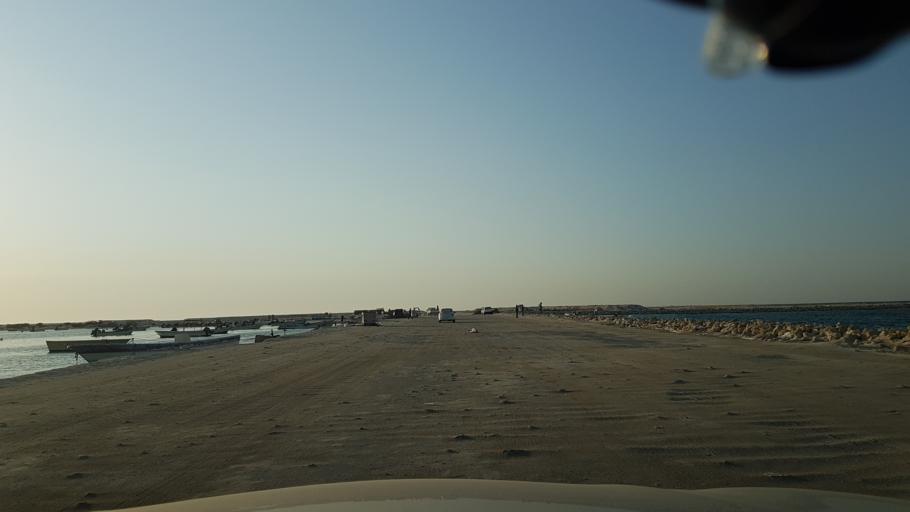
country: BH
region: Manama
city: Jidd Hafs
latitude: 26.2534
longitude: 50.5009
